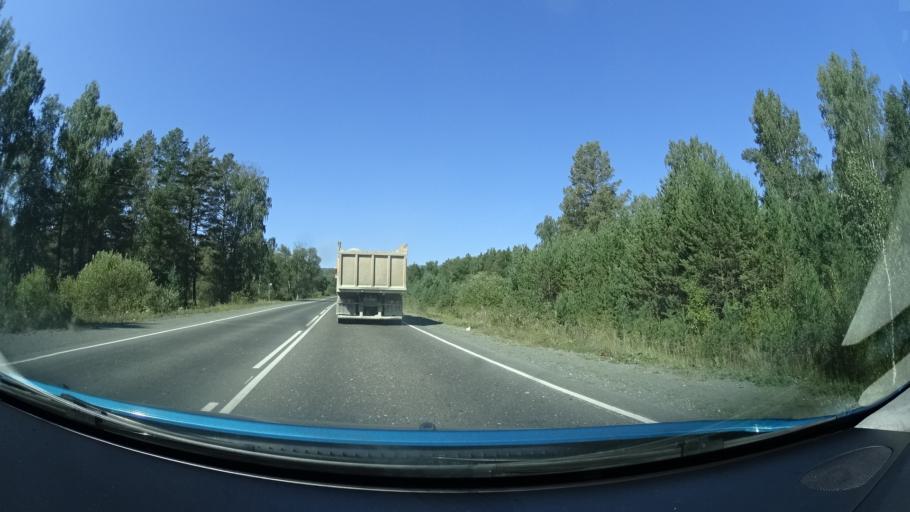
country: RU
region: Bashkortostan
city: Abzakovo
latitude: 53.8614
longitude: 58.5509
